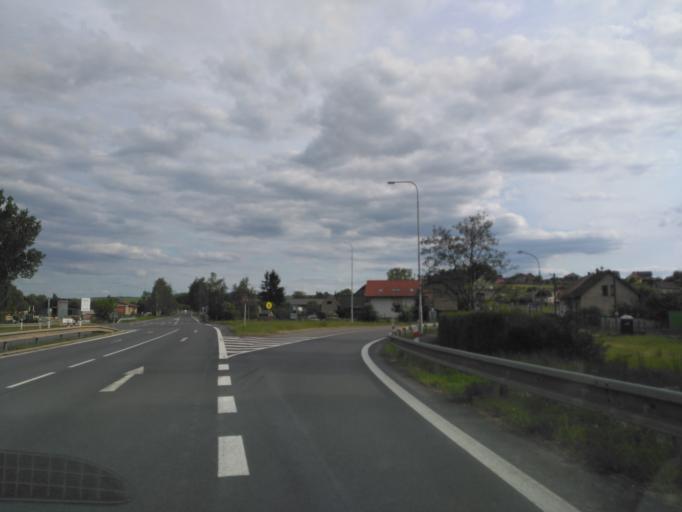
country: CZ
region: Central Bohemia
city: Zdice
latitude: 49.9014
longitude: 13.9613
